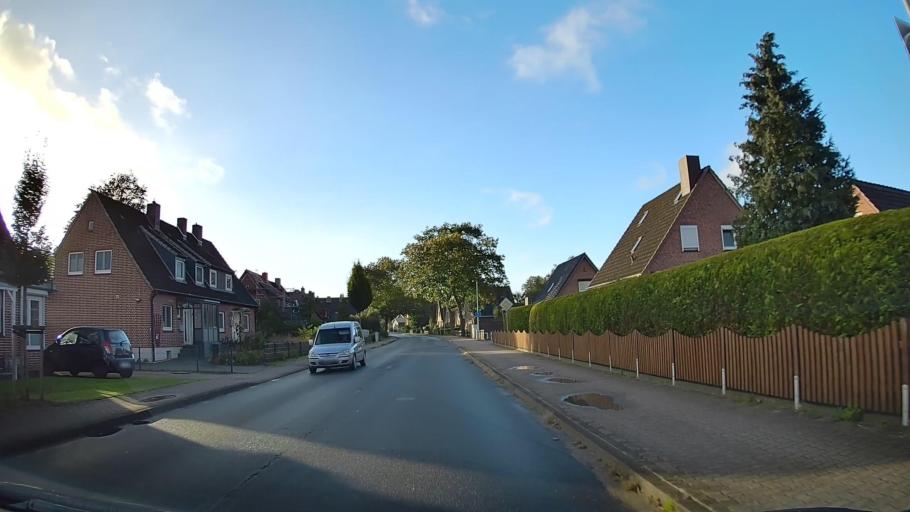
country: DE
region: Schleswig-Holstein
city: Horst
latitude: 53.8112
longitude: 9.6298
